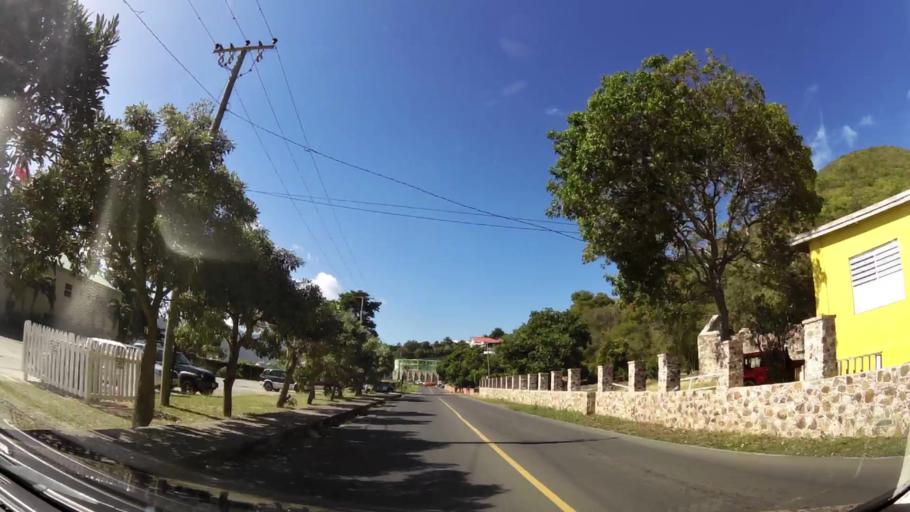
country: VG
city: Tortola
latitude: 18.4157
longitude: -64.5952
